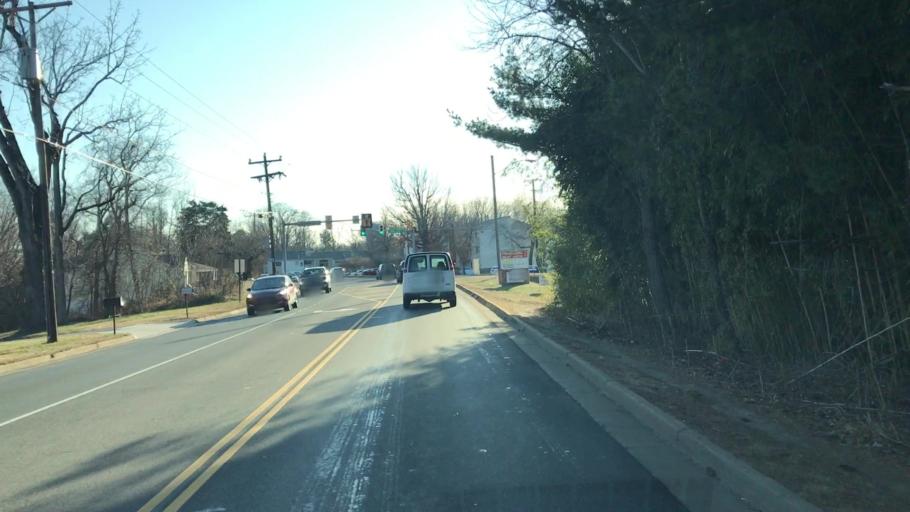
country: US
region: Virginia
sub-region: City of Fredericksburg
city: Fredericksburg
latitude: 38.2832
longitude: -77.4806
